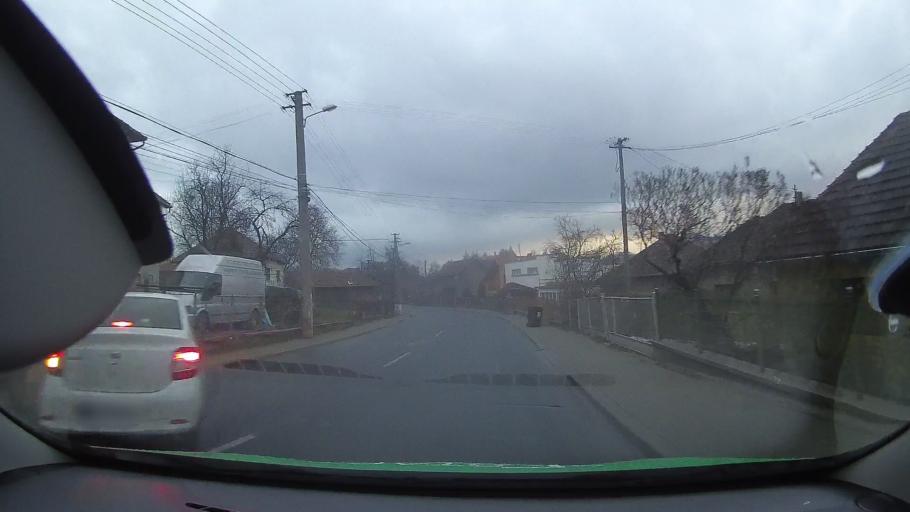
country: RO
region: Hunedoara
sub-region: Municipiul Brad
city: Brad
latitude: 46.1276
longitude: 22.7856
